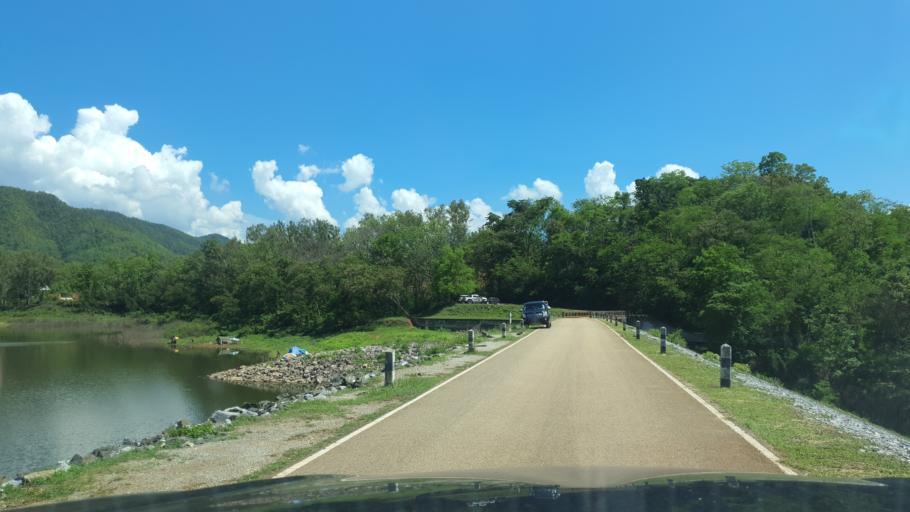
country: TH
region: Chiang Mai
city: Mae On
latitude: 18.8068
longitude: 99.2647
